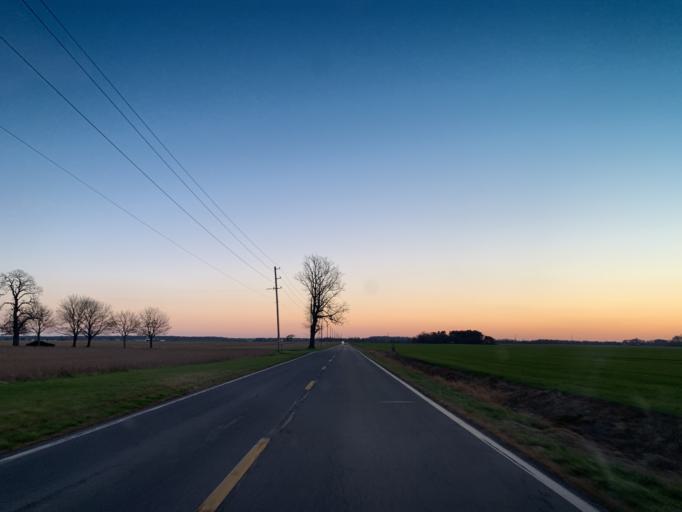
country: US
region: Delaware
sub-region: New Castle County
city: Middletown
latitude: 39.4167
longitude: -75.7448
